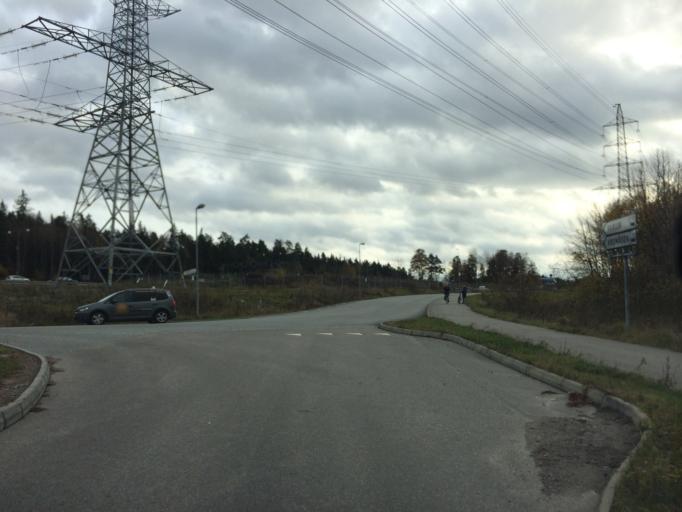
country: SE
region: Stockholm
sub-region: Sollentuna Kommun
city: Sollentuna
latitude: 59.4341
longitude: 17.9209
